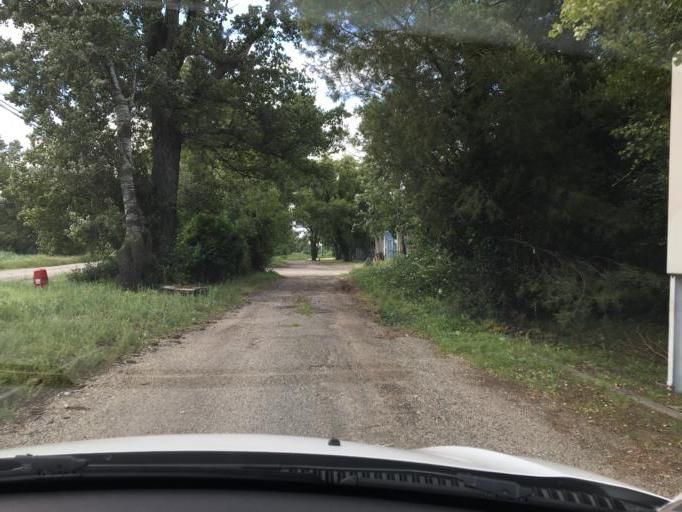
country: FR
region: Provence-Alpes-Cote d'Azur
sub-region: Departement du Vaucluse
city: Bollene
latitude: 44.3096
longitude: 4.7351
